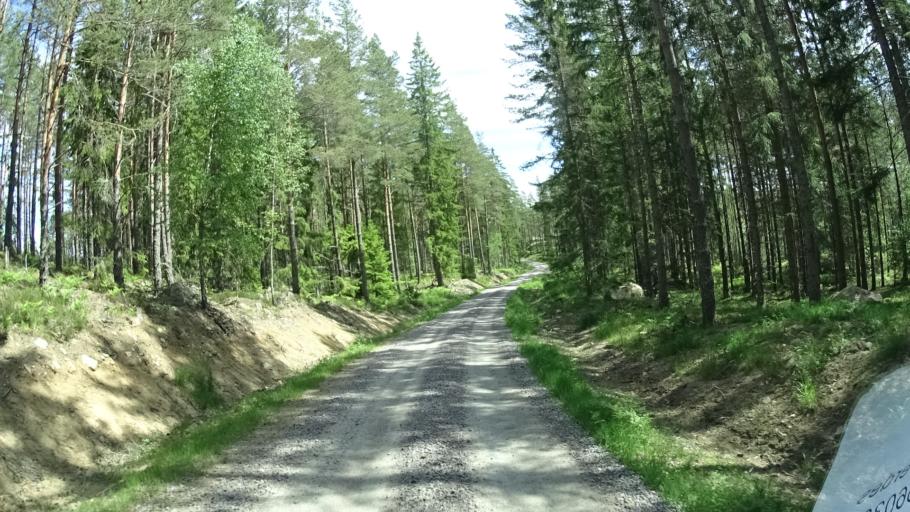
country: SE
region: OEstergoetland
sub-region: Norrkopings Kommun
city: Svartinge
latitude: 58.7712
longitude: 15.9452
